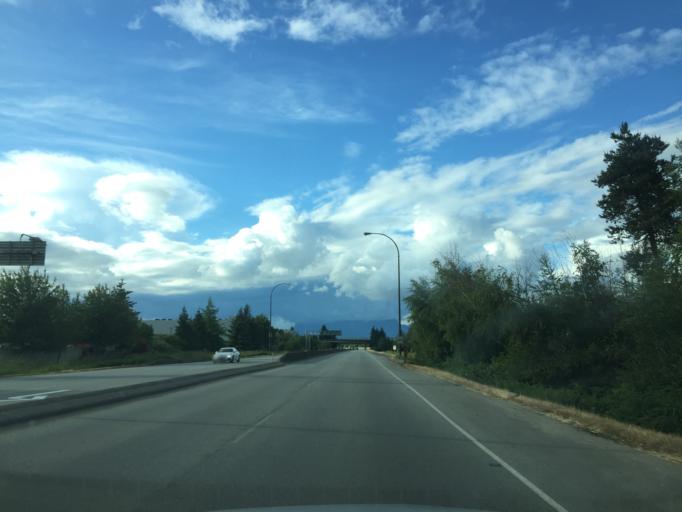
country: CA
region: British Columbia
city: Richmond
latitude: 49.1709
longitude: -123.0744
